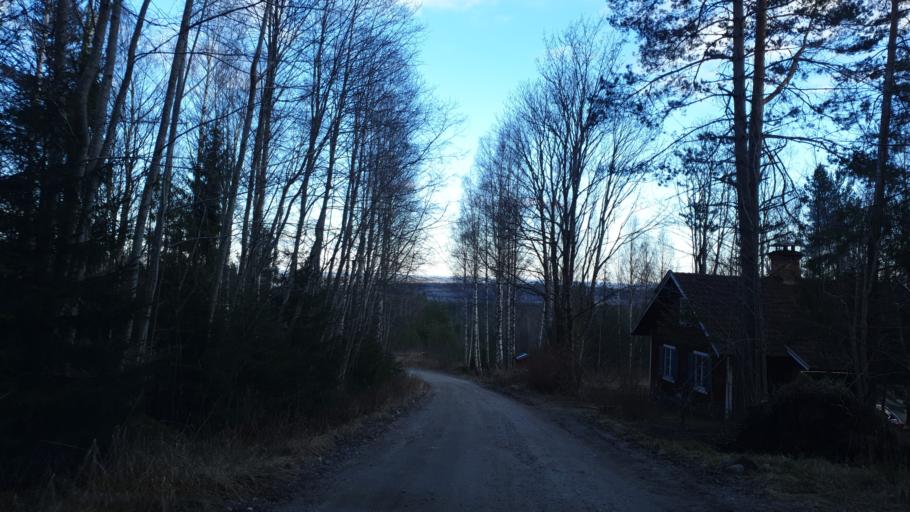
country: SE
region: OErebro
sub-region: Orebro Kommun
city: Garphyttan
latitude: 59.3628
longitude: 14.9720
